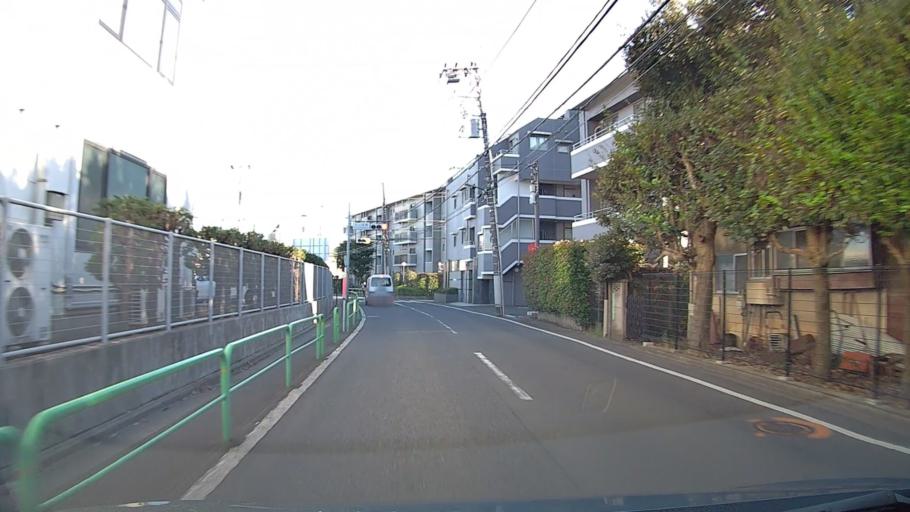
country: JP
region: Tokyo
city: Nishi-Tokyo-shi
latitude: 35.7551
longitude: 139.5759
